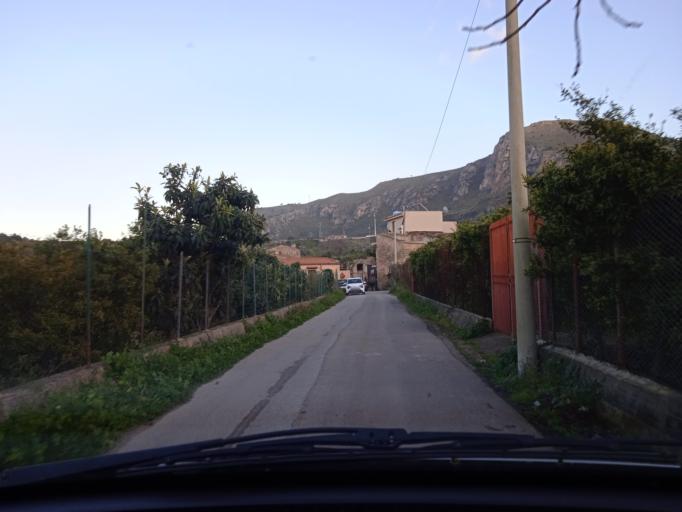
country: IT
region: Sicily
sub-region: Palermo
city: Villabate
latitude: 38.0766
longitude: 13.4270
